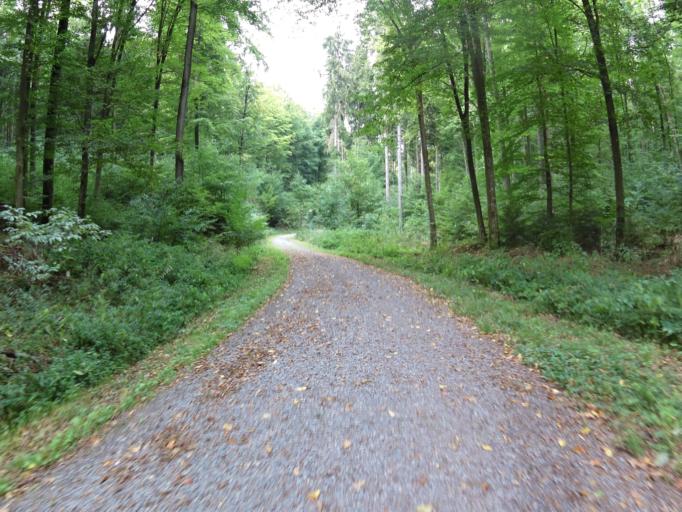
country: DE
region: Bavaria
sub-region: Regierungsbezirk Unterfranken
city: Waldbrunn
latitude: 49.7688
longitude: 9.7972
